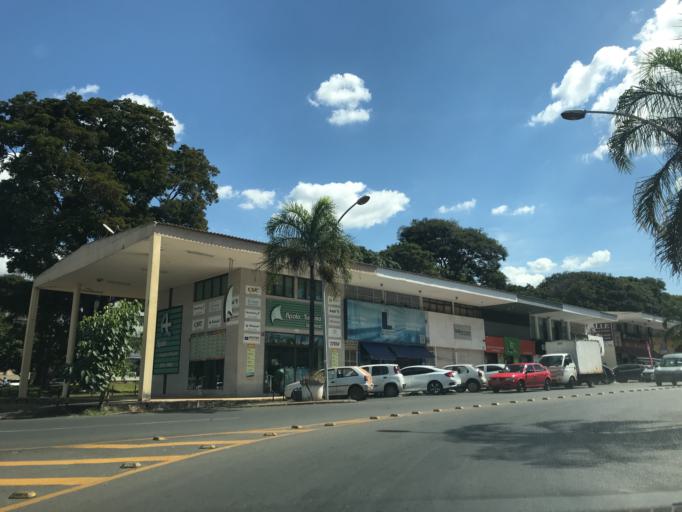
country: BR
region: Federal District
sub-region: Brasilia
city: Brasilia
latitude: -15.8353
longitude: -47.9165
